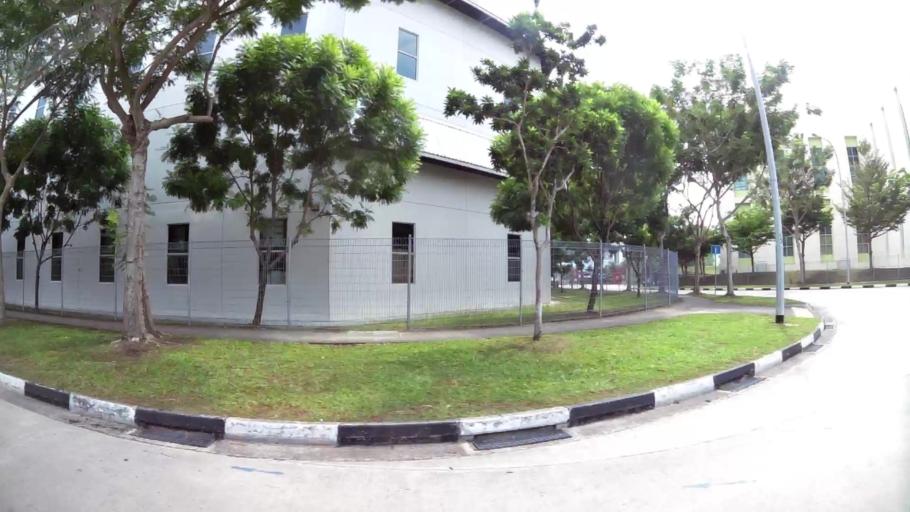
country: SG
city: Singapore
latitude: 1.3522
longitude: 103.9704
